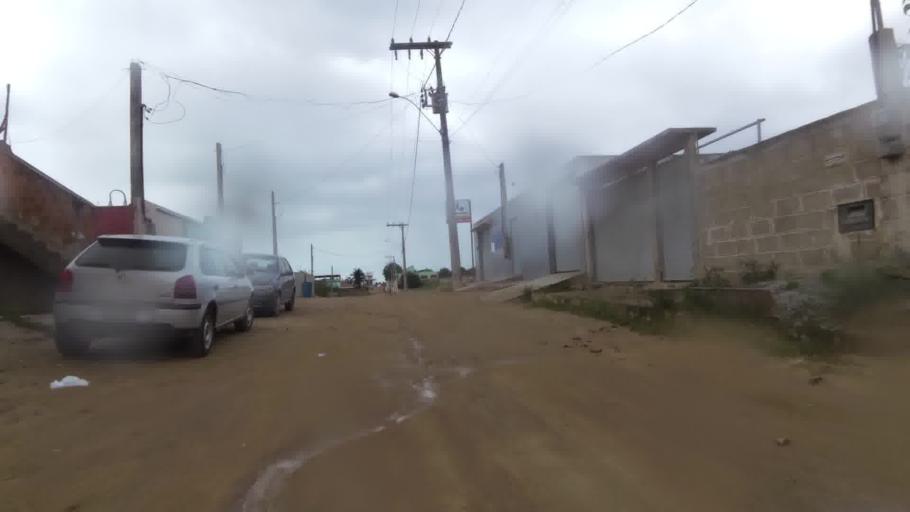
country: BR
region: Espirito Santo
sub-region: Marataizes
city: Marataizes
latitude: -21.0430
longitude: -40.8413
